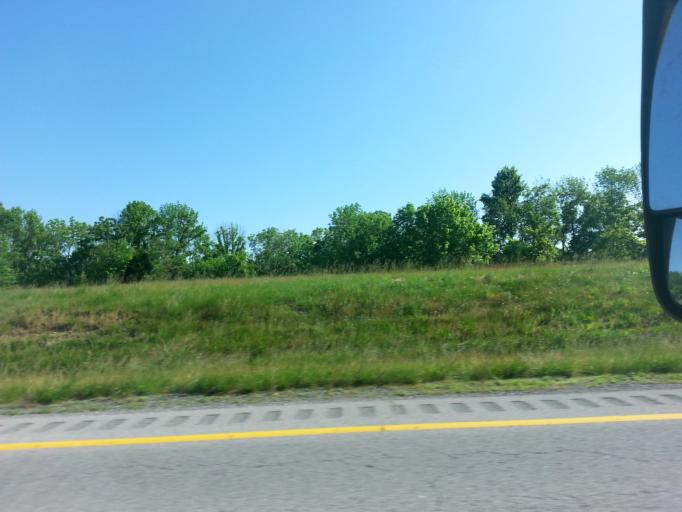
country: US
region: Kentucky
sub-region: Shelby County
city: Shelbyville
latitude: 38.1781
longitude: -85.1717
